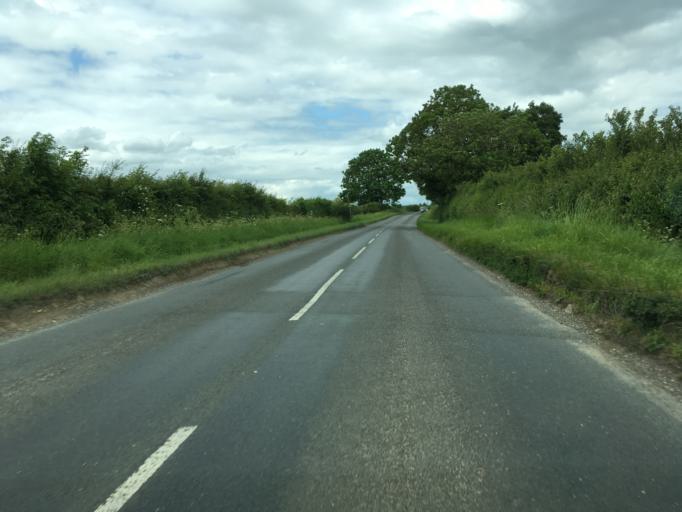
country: GB
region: England
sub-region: Gloucestershire
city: Cirencester
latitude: 51.6910
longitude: -1.9670
